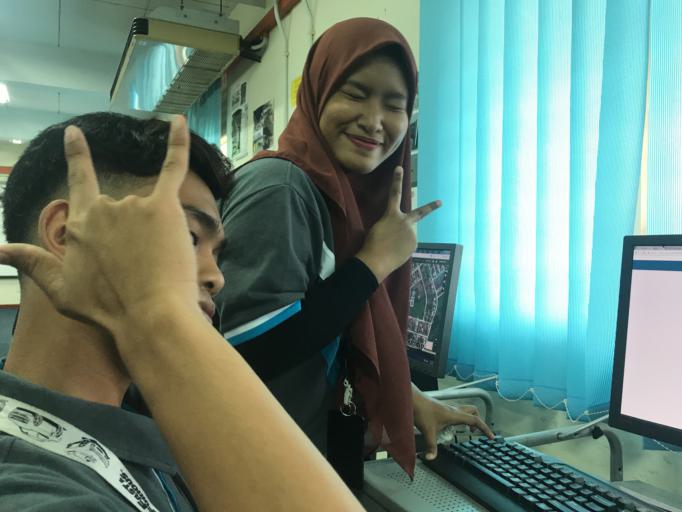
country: MY
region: Perak
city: Ipoh
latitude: 4.5887
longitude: 101.1247
